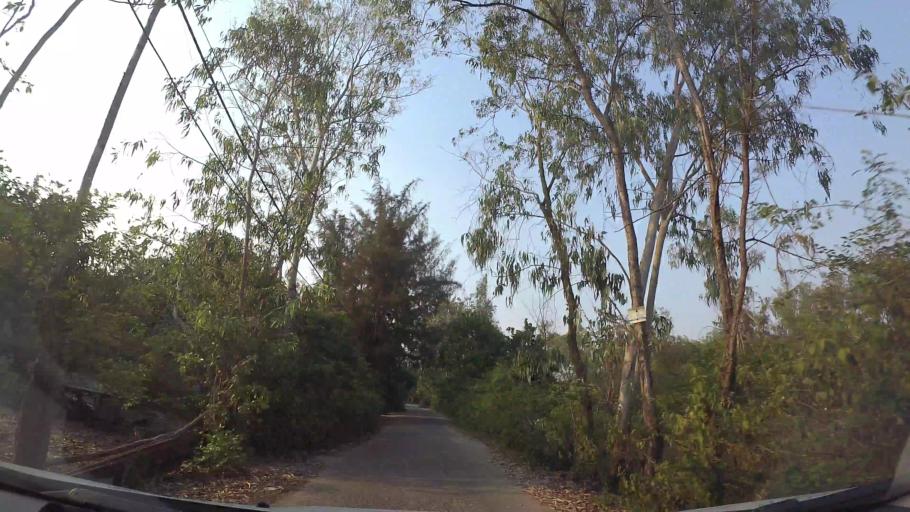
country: VN
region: Da Nang
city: Ngu Hanh Son
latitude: 15.9722
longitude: 108.2437
